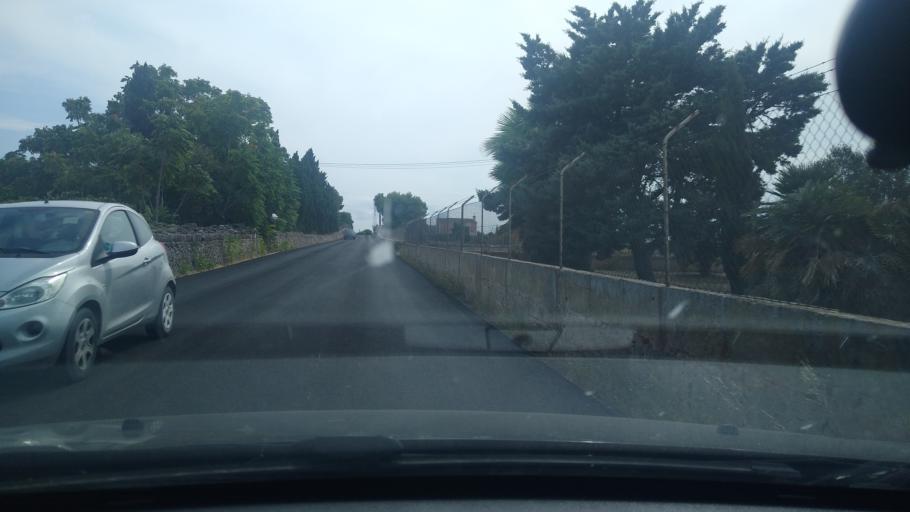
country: ES
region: Balearic Islands
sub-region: Illes Balears
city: Santa Margalida
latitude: 39.7297
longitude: 3.1176
